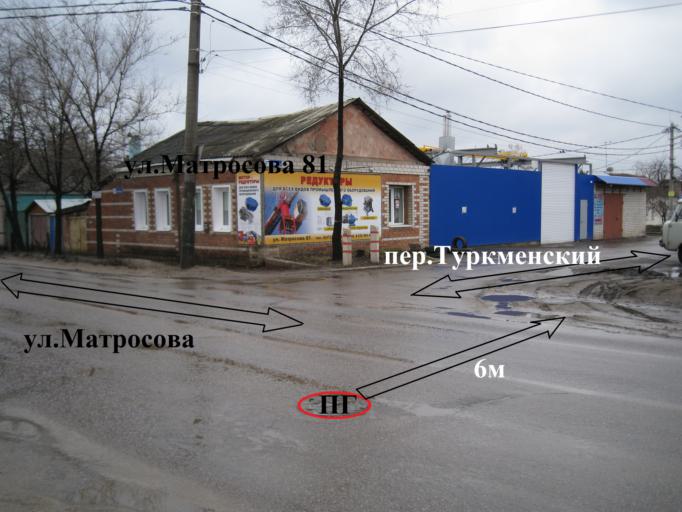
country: RU
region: Voronezj
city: Voronezh
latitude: 51.6363
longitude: 39.1700
